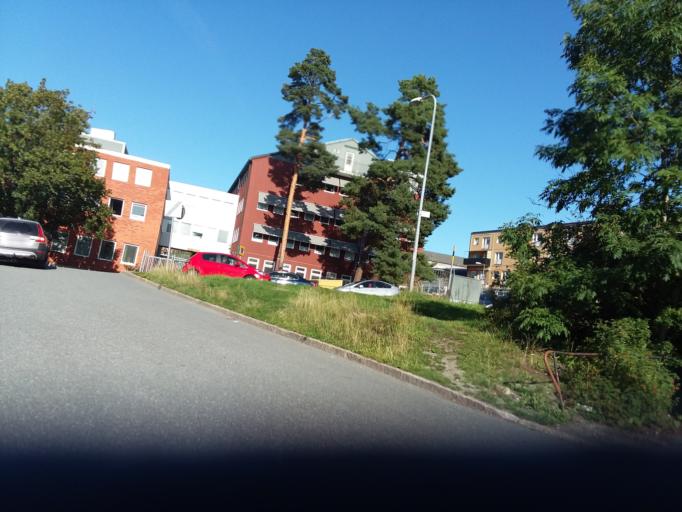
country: SE
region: Stockholm
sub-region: Stockholms Kommun
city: Bromma
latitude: 59.3479
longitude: 17.8813
